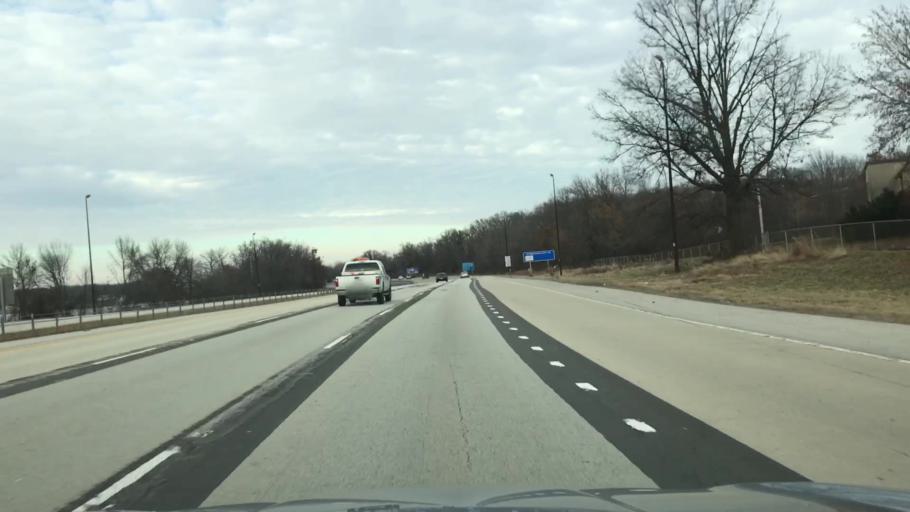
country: US
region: Illinois
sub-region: Sangamon County
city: Chatham
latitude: 39.6900
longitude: -89.6430
